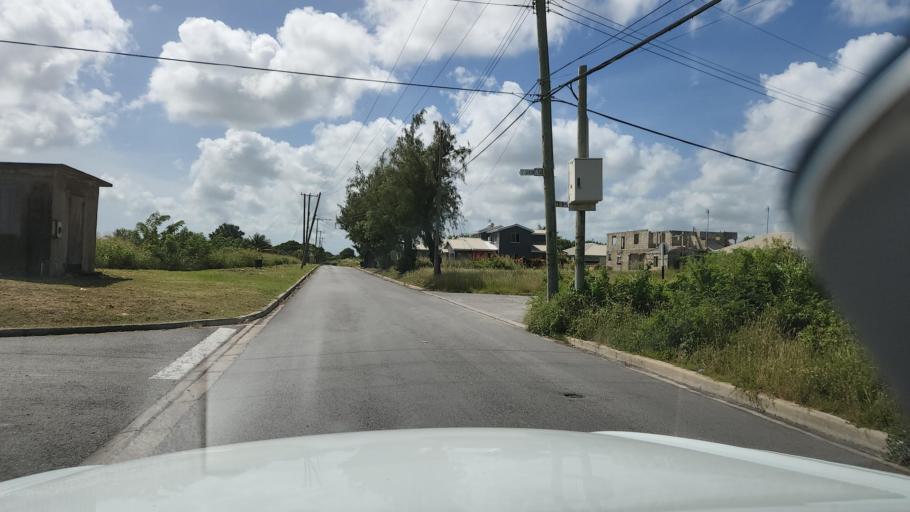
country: BB
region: Saint Philip
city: Crane
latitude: 13.1616
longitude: -59.4438
